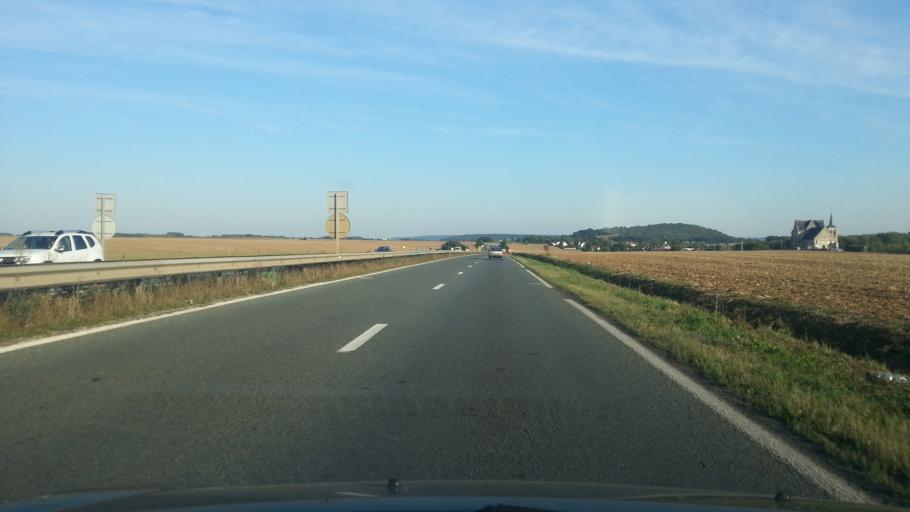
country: FR
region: Picardie
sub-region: Departement de l'Oise
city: Allonne
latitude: 49.4253
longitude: 2.1390
